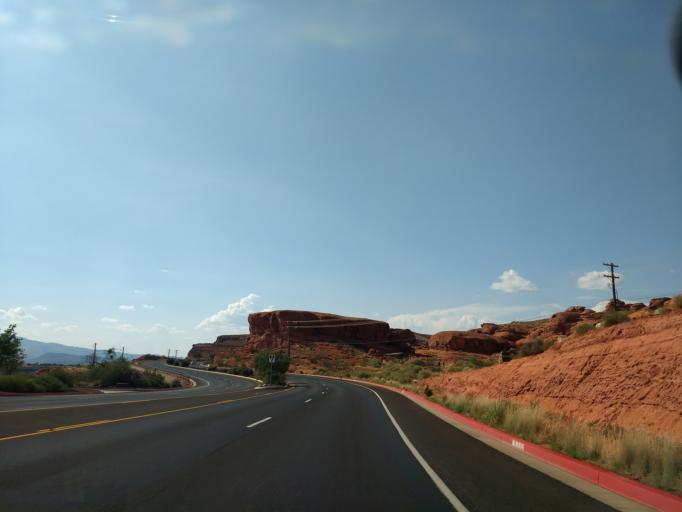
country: US
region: Utah
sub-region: Washington County
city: Saint George
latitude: 37.1142
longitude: -113.5775
